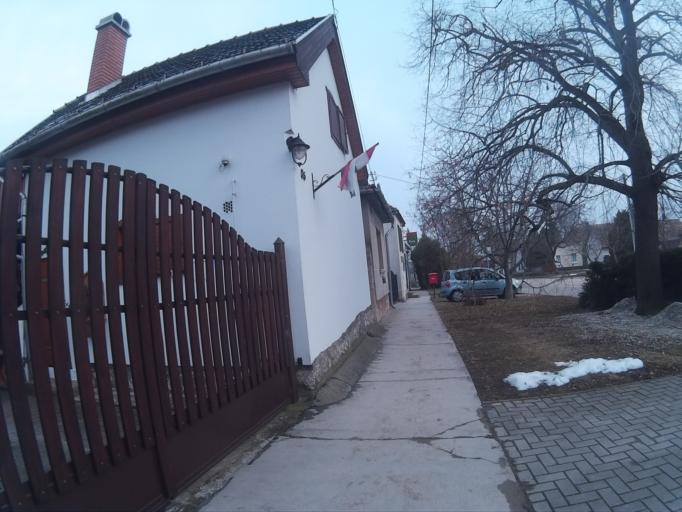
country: HU
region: Komarom-Esztergom
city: Tarjan
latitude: 47.6458
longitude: 18.5129
